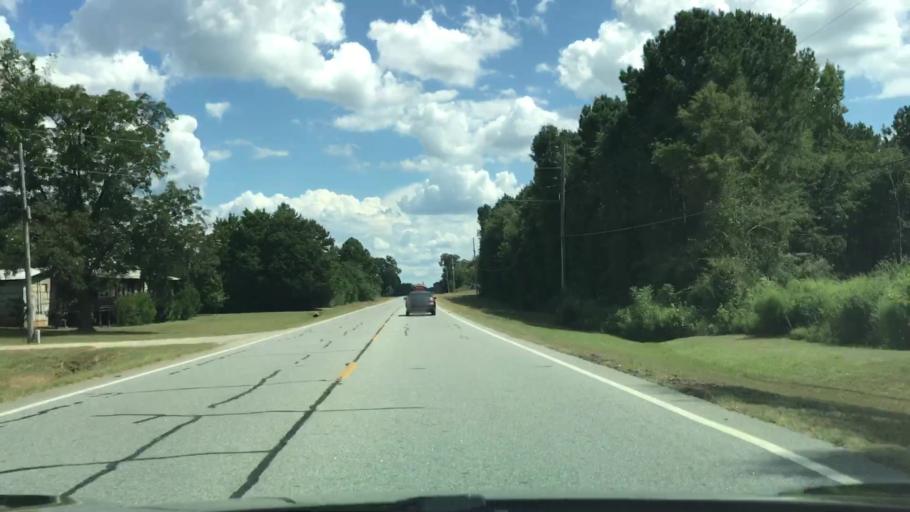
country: US
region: Georgia
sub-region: Oconee County
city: Watkinsville
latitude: 33.8059
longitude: -83.3459
